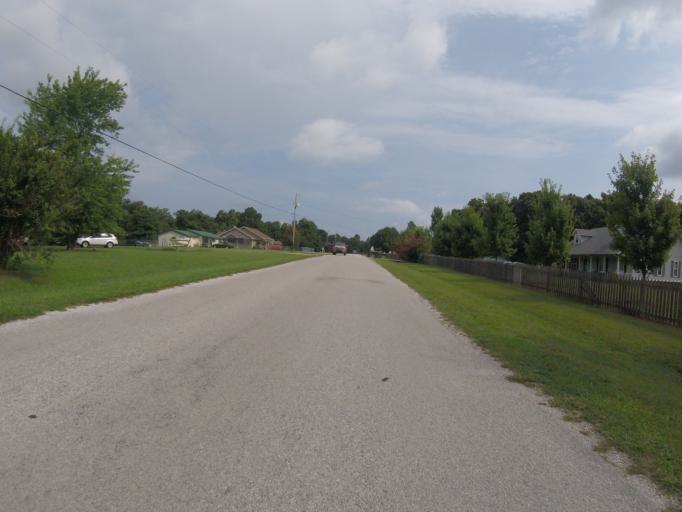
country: US
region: Arkansas
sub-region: Washington County
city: Farmington
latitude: 36.0837
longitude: -94.2992
